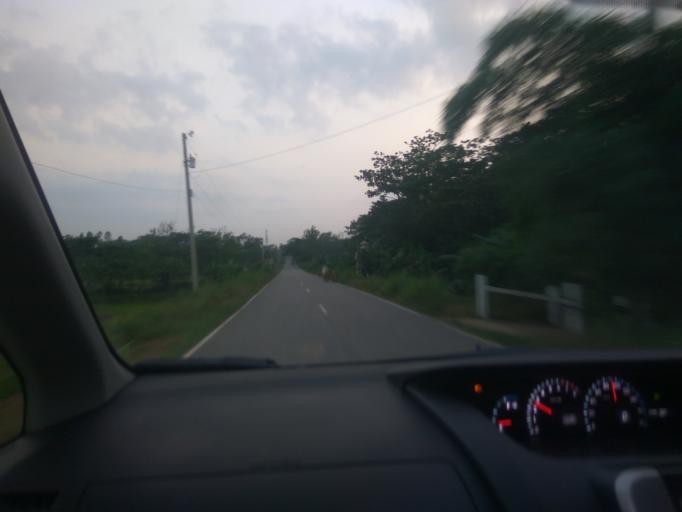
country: IN
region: Assam
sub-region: Karimganj
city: Karimganj
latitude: 24.9454
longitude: 92.2342
